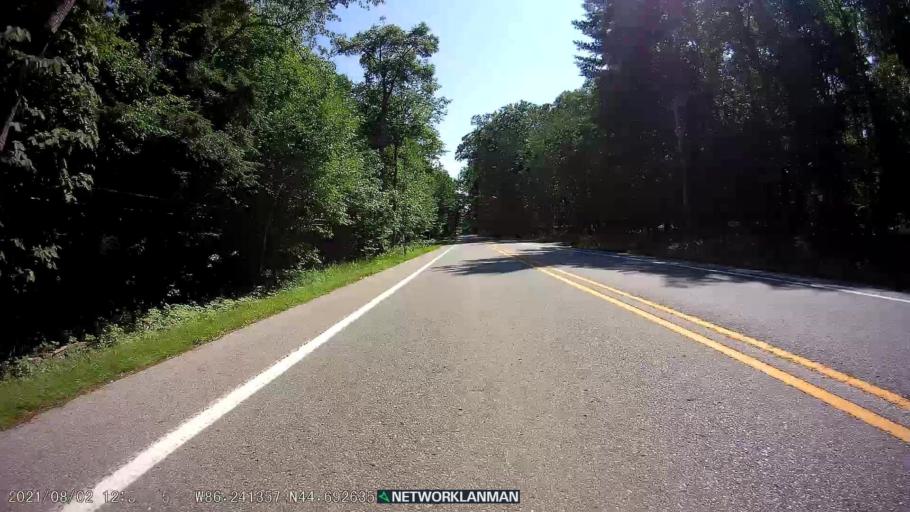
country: US
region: Michigan
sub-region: Benzie County
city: Frankfort
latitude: 44.6926
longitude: -86.2414
